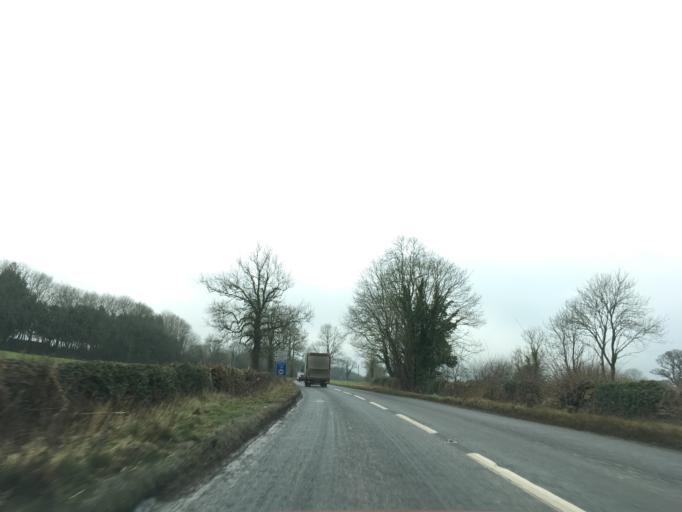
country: GB
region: England
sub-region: Gloucestershire
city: Tetbury
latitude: 51.6654
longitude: -2.1106
